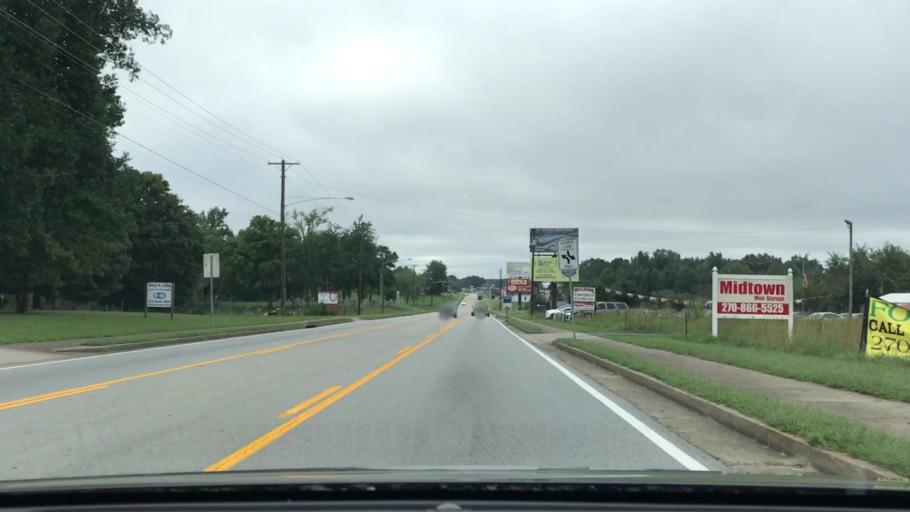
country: US
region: Kentucky
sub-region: Russell County
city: Jamestown
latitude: 37.0191
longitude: -85.0762
